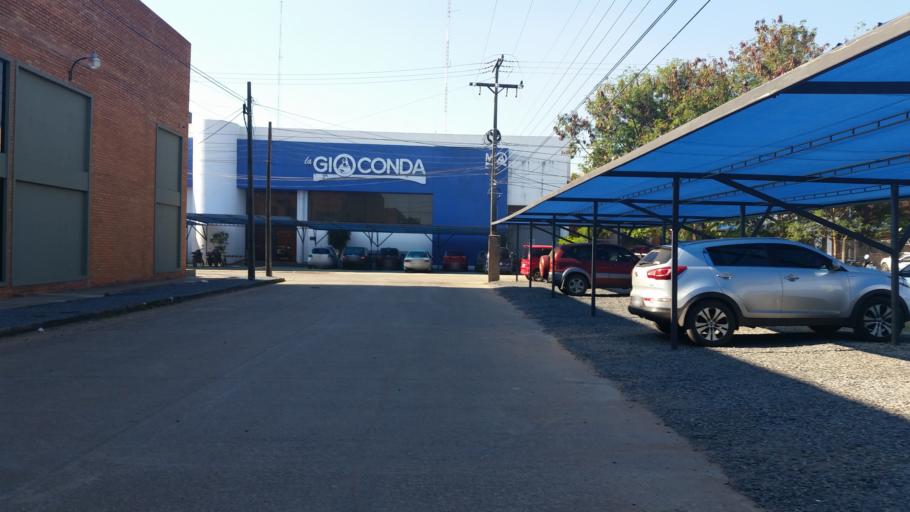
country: PY
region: Asuncion
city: Asuncion
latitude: -25.2711
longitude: -57.6073
